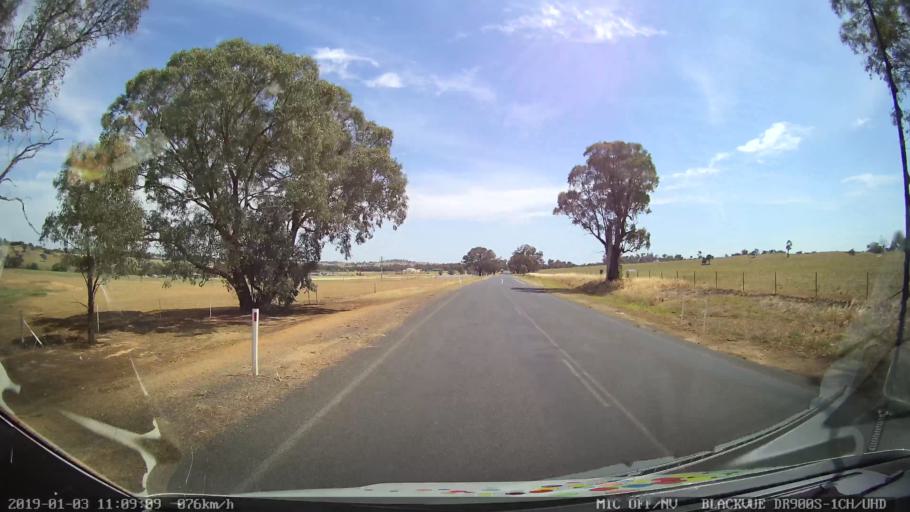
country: AU
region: New South Wales
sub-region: Young
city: Young
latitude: -34.2416
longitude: 148.2553
